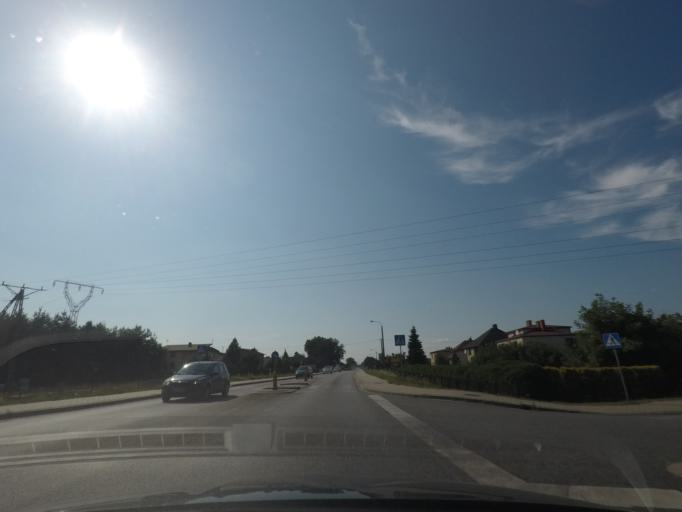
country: PL
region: Silesian Voivodeship
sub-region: Powiat pszczynski
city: Suszec
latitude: 50.0294
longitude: 18.7914
